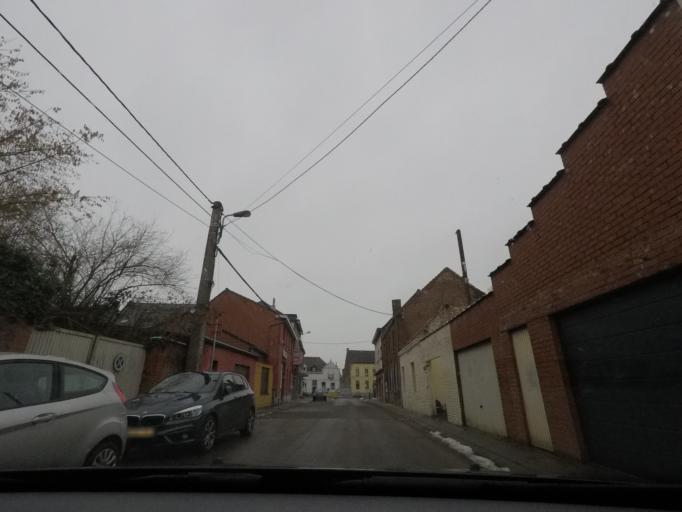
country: BE
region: Wallonia
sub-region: Province du Hainaut
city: Brugelette
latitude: 50.5955
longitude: 3.8536
